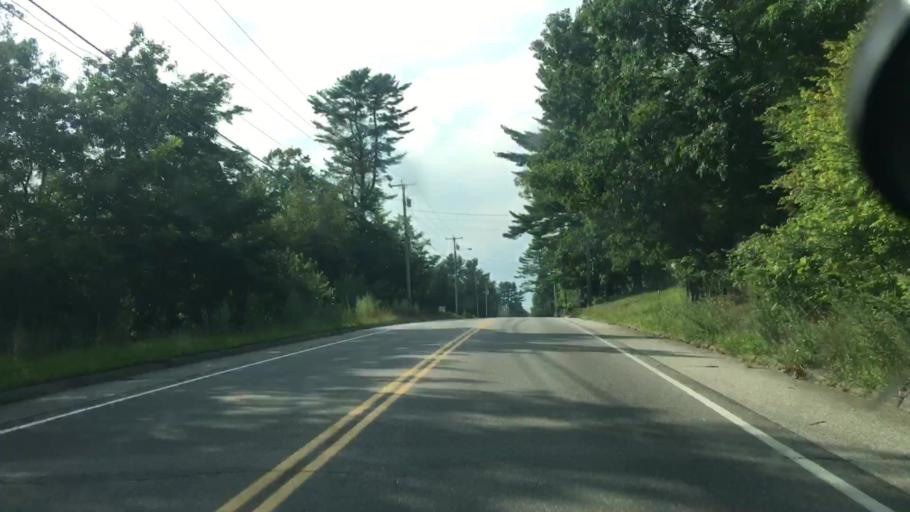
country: US
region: Maine
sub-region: Cumberland County
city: North Windham
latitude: 43.8143
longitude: -70.4260
